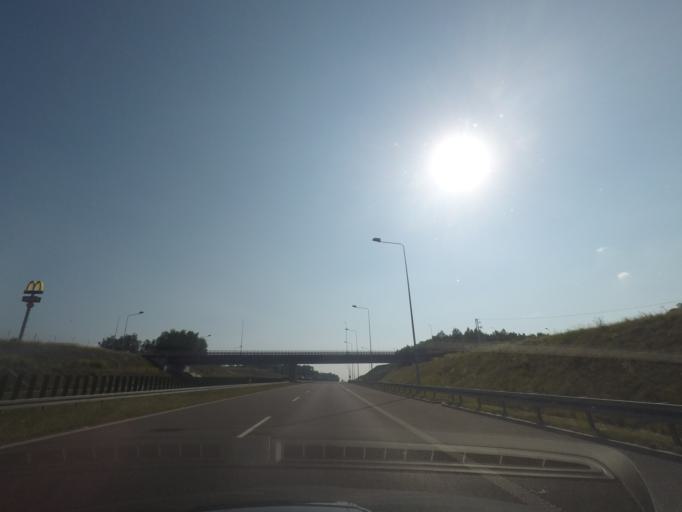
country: PL
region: Silesian Voivodeship
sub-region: Powiat wodzislawski
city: Laziska
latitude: 49.9455
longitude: 18.4298
